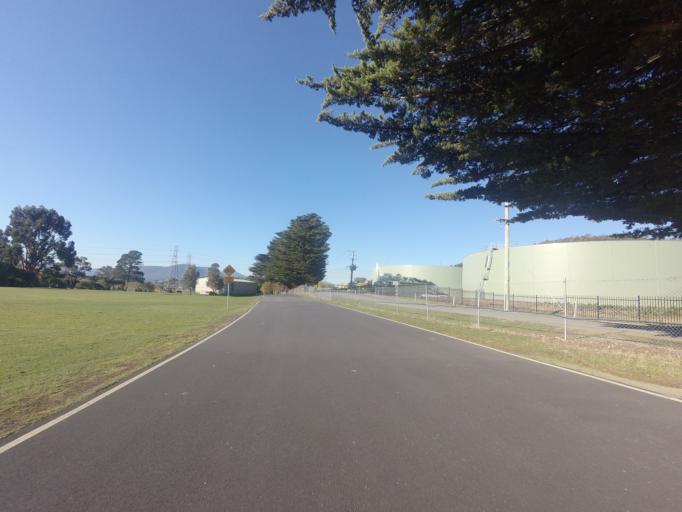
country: AU
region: Tasmania
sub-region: Glenorchy
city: West Moonah
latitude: -42.8536
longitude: 147.2516
